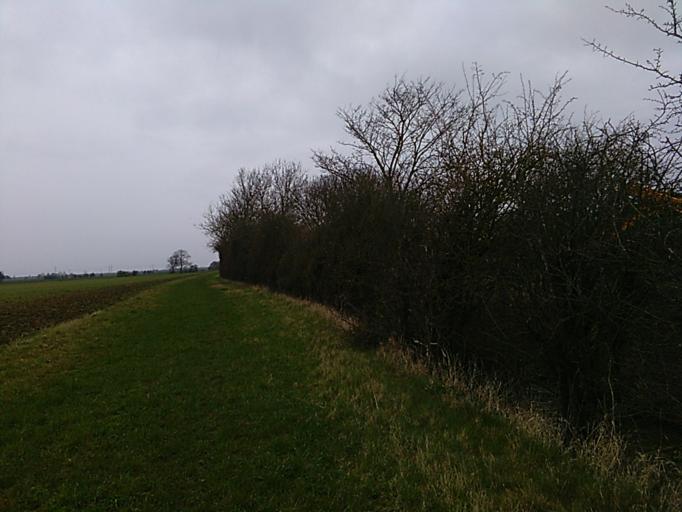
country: GB
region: England
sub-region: Nottinghamshire
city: Bingham
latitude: 52.9162
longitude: -0.9350
